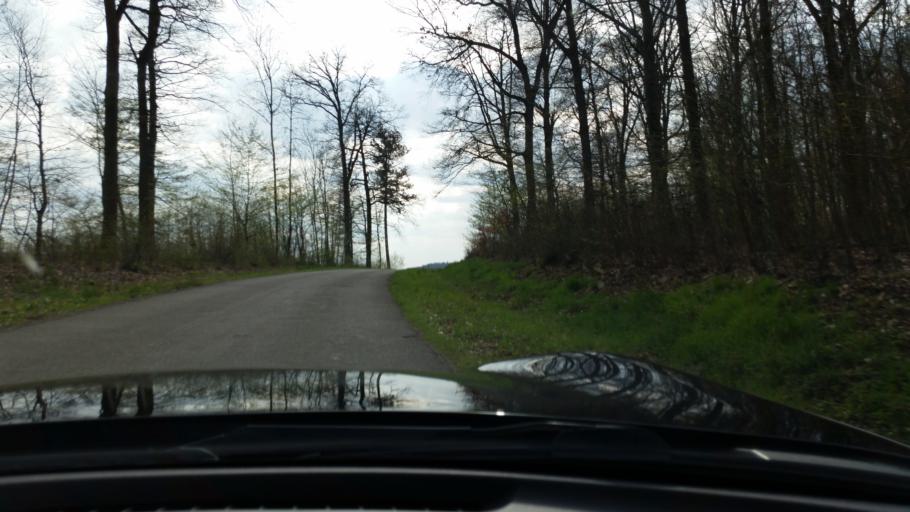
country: DE
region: Baden-Wuerttemberg
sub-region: Regierungsbezirk Stuttgart
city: Widdern
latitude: 49.3607
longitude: 9.4307
